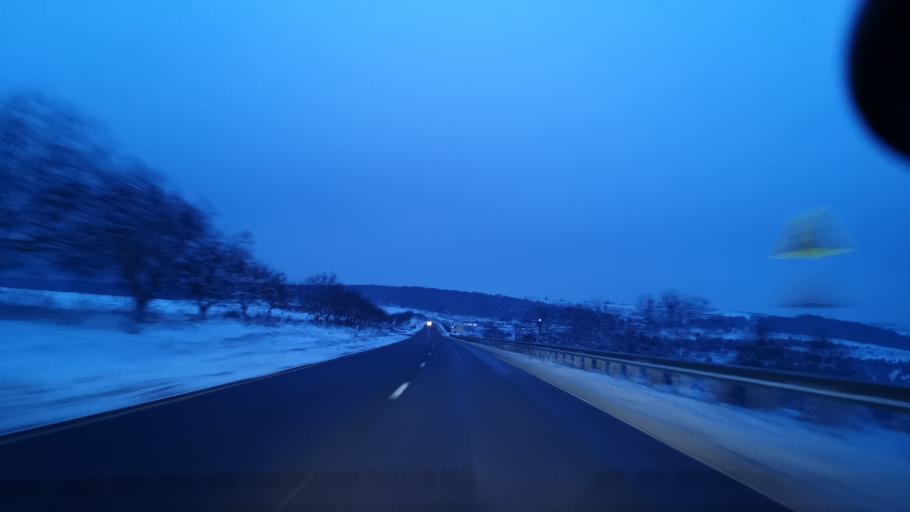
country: MD
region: Rezina
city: Saharna
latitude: 47.6069
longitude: 28.8305
